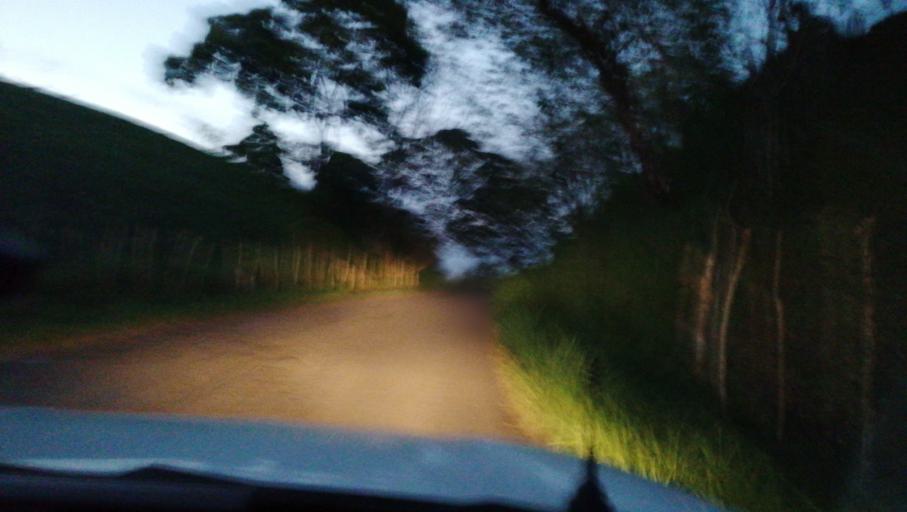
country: MX
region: Chiapas
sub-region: Ostuacan
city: Nuevo Juan del Grijalva
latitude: 17.4787
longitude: -93.3467
